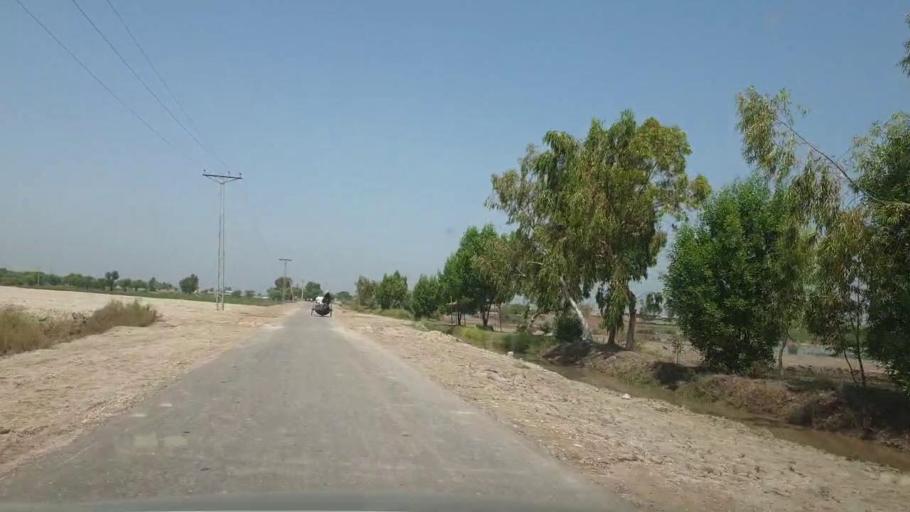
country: PK
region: Sindh
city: Warah
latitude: 27.4768
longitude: 67.7577
